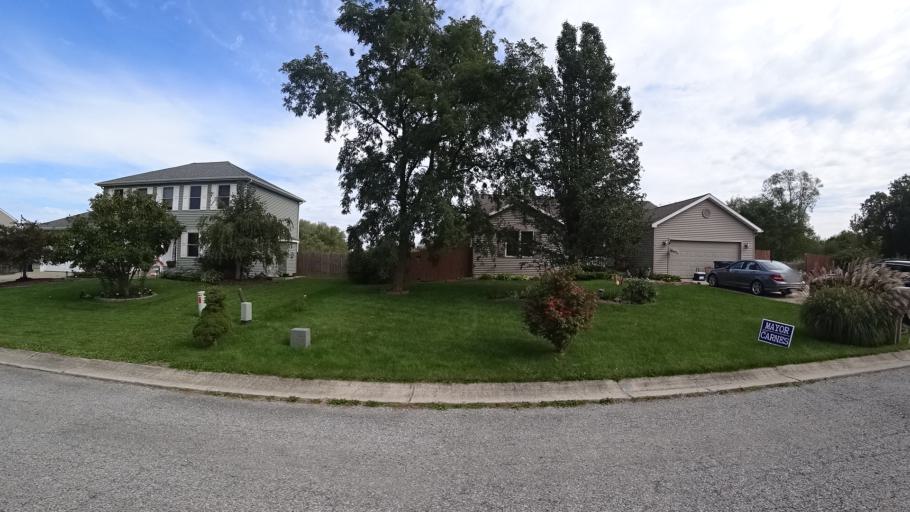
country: US
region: Indiana
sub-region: LaPorte County
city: Long Beach
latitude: 41.7227
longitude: -86.8450
